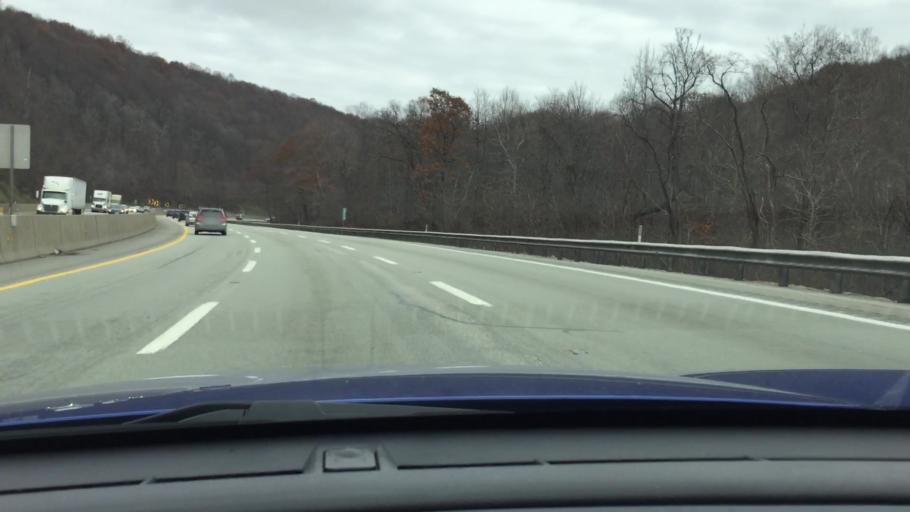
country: US
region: Pennsylvania
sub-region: Fayette County
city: Bear Rocks
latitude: 40.1512
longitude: -79.4469
